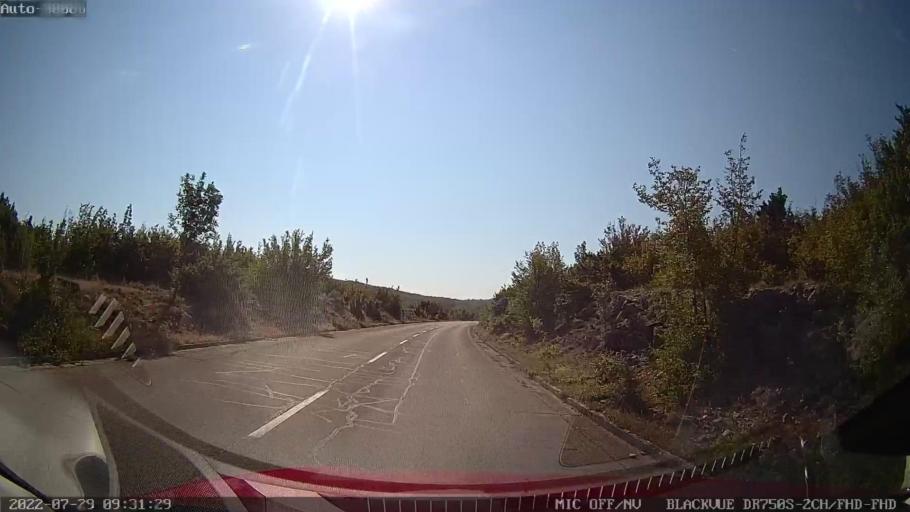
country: HR
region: Zadarska
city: Obrovac
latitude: 44.1889
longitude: 15.6998
